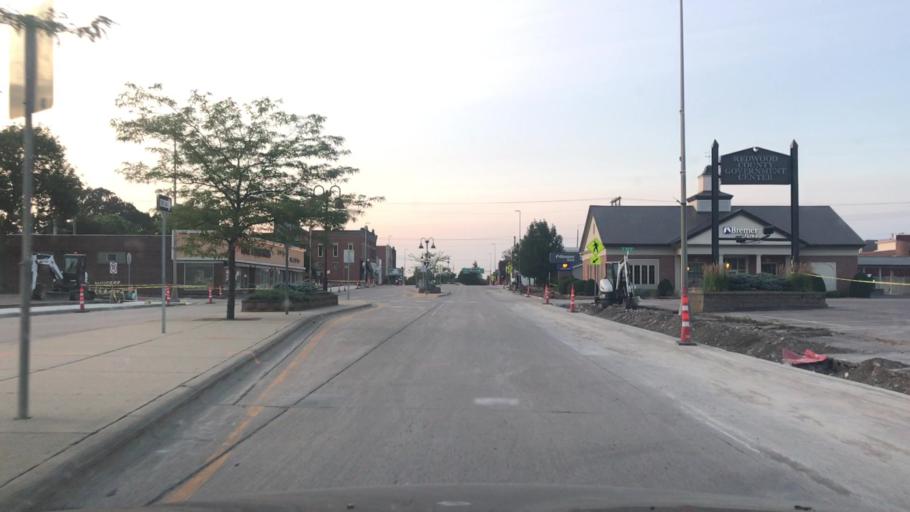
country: US
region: Minnesota
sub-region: Redwood County
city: Redwood Falls
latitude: 44.5381
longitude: -95.1194
